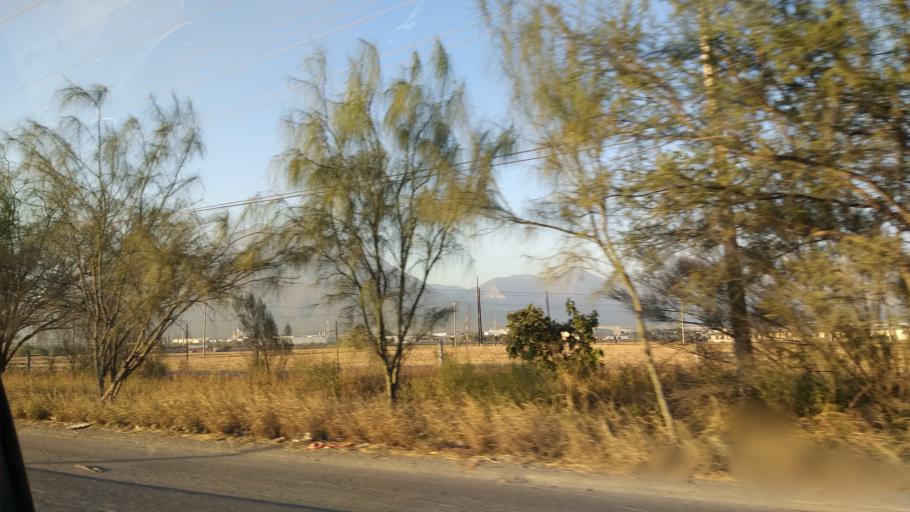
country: MX
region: Nuevo Leon
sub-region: Garcia
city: Parque Industrial Ciudad Mitras
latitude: 25.7770
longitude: -100.4404
